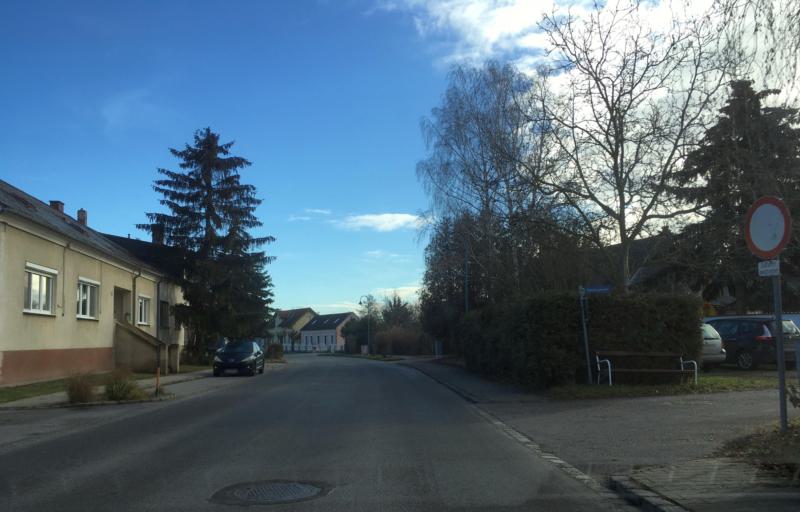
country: AT
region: Lower Austria
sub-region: Politischer Bezirk Ganserndorf
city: Eckartsau
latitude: 48.1445
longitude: 16.7999
